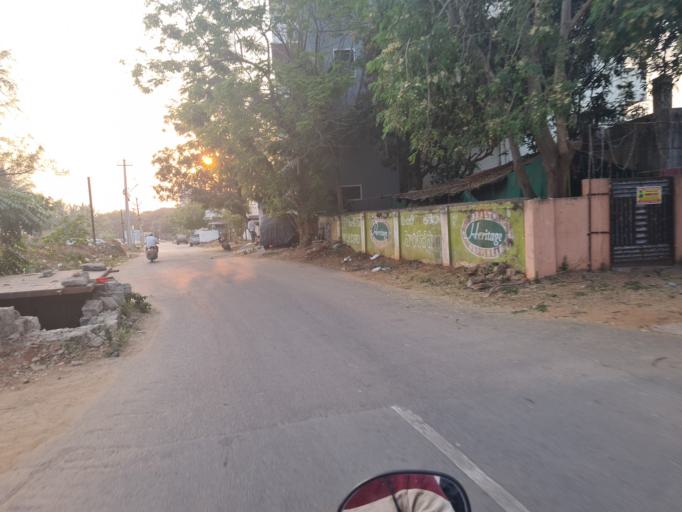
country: IN
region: Telangana
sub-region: Medak
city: Serilingampalle
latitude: 17.4791
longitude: 78.2995
